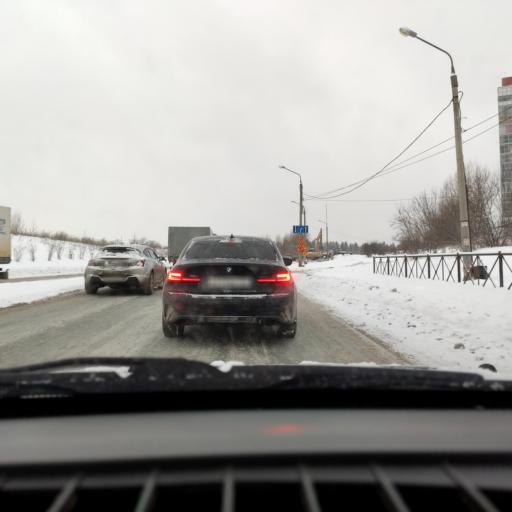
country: RU
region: Perm
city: Perm
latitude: 57.9628
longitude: 56.2038
